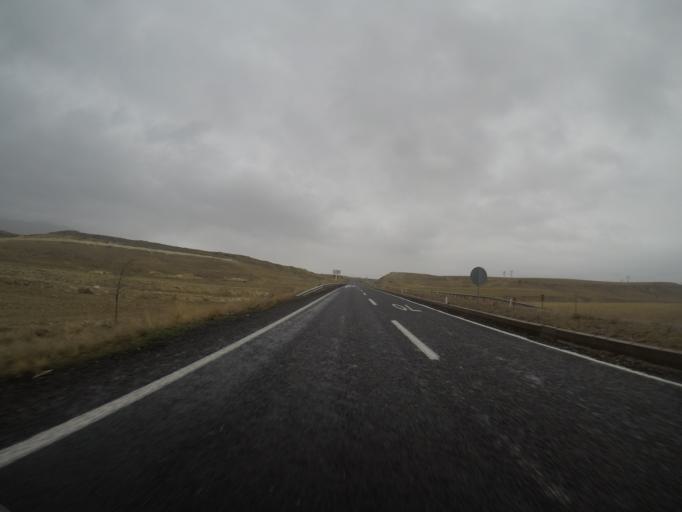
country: TR
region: Nevsehir
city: Avanos
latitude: 38.7045
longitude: 34.8712
